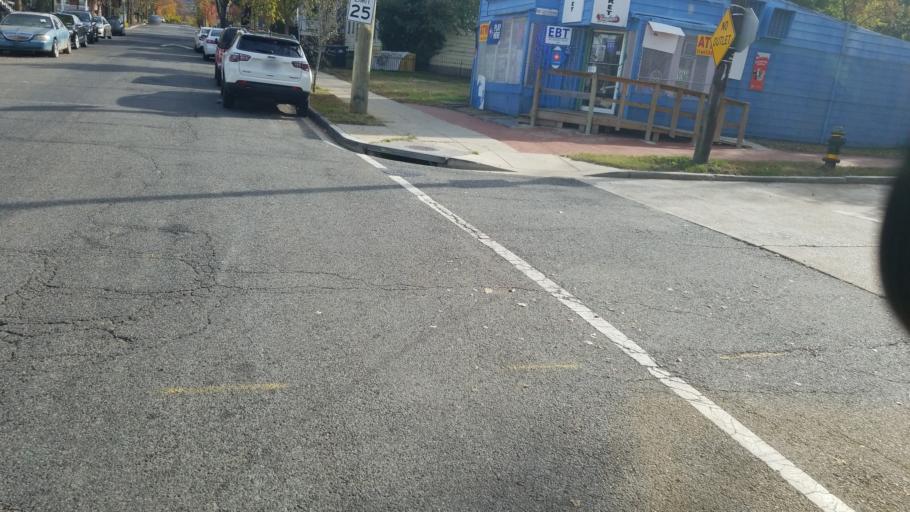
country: US
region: Maryland
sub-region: Prince George's County
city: Hillcrest Heights
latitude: 38.8644
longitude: -76.9869
